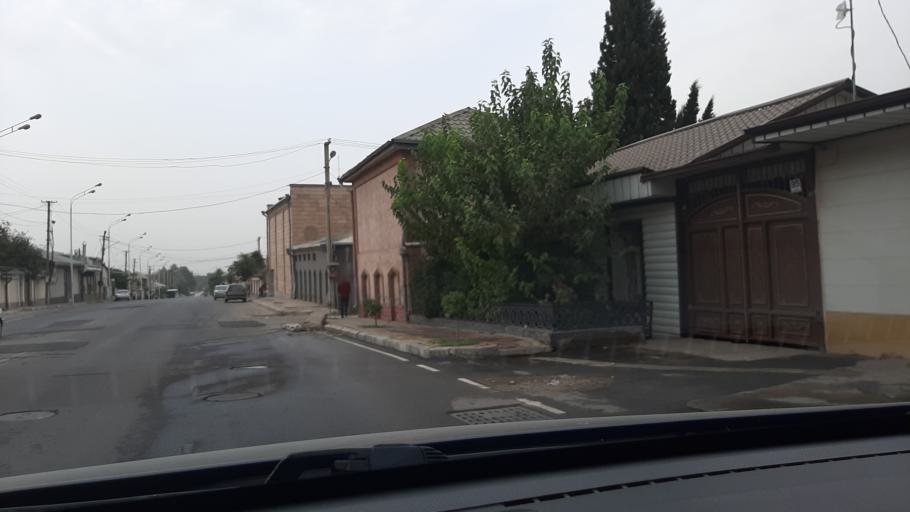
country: TJ
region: Dushanbe
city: Dushanbe
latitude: 38.6133
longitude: 68.7826
